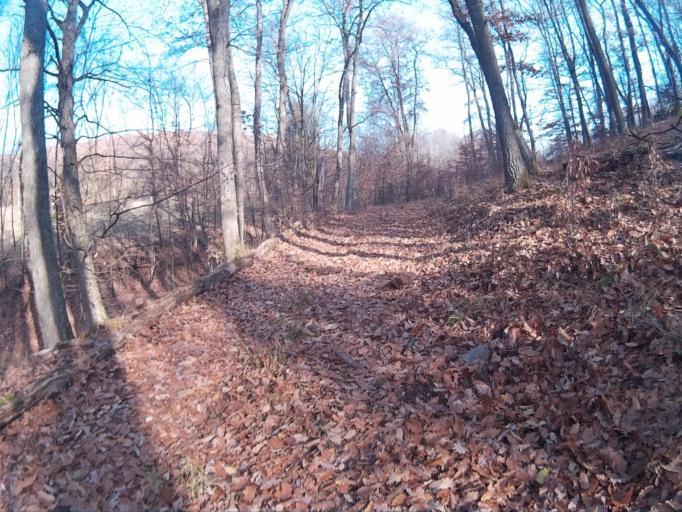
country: HU
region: Heves
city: Felsotarkany
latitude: 48.0023
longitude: 20.3945
